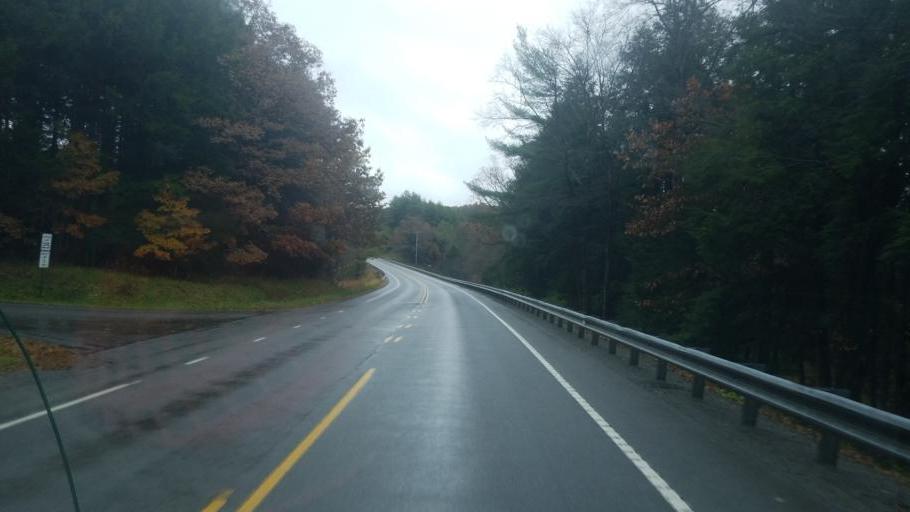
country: US
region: Pennsylvania
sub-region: Clearfield County
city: Shiloh
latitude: 41.1011
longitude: -78.2100
